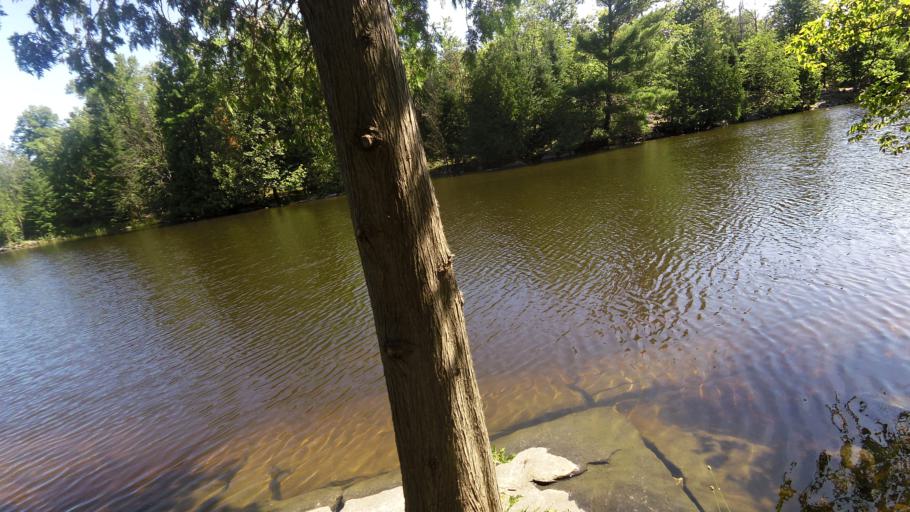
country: CA
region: Ontario
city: Arnprior
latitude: 45.4632
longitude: -76.2613
